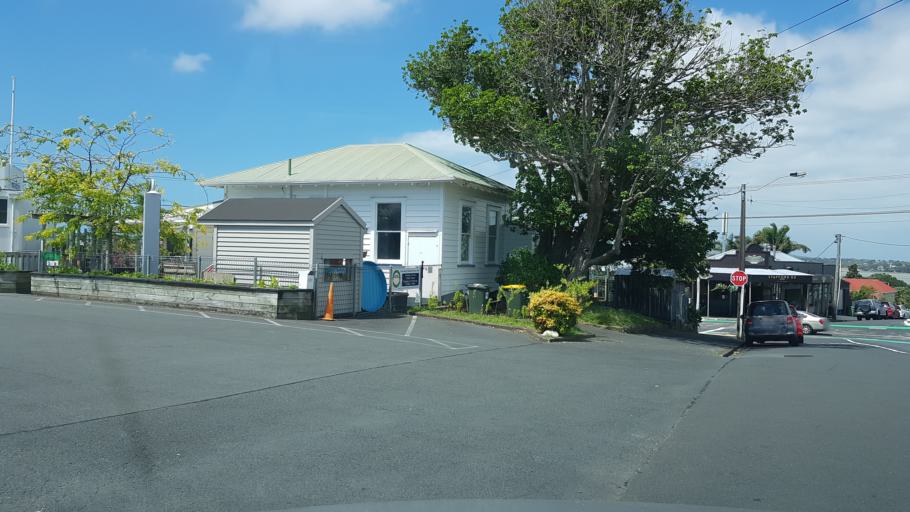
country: NZ
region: Auckland
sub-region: Auckland
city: North Shore
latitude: -36.8161
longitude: 174.7449
